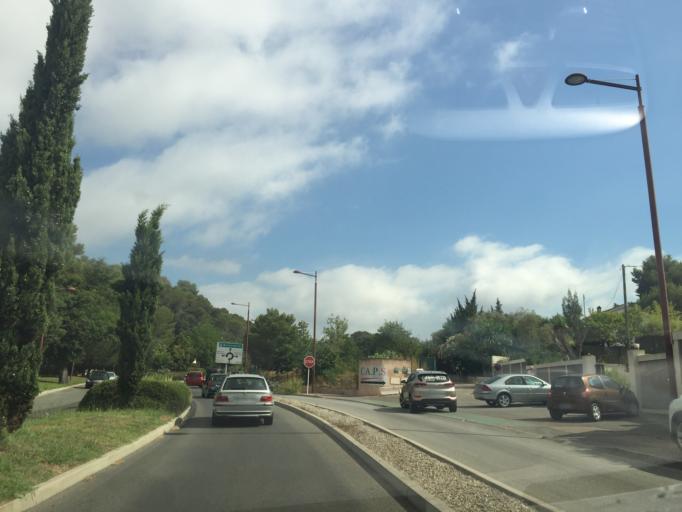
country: FR
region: Provence-Alpes-Cote d'Azur
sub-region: Departement des Alpes-Maritimes
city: Vallauris
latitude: 43.5842
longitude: 7.0901
